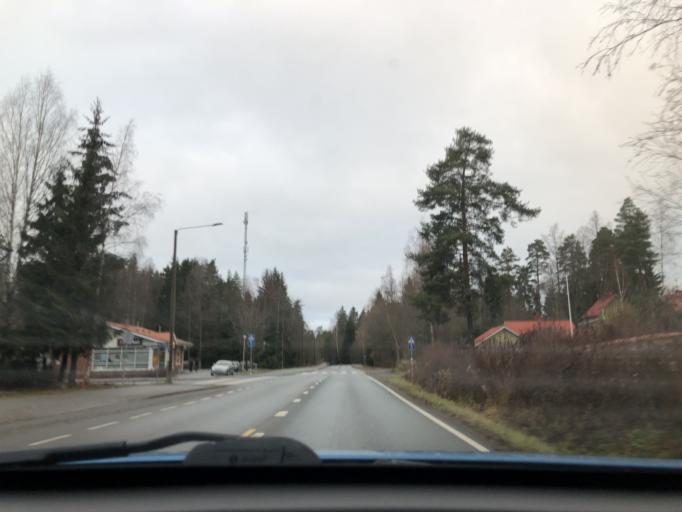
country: FI
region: Pirkanmaa
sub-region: Tampere
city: Kangasala
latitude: 61.5267
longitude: 24.0188
